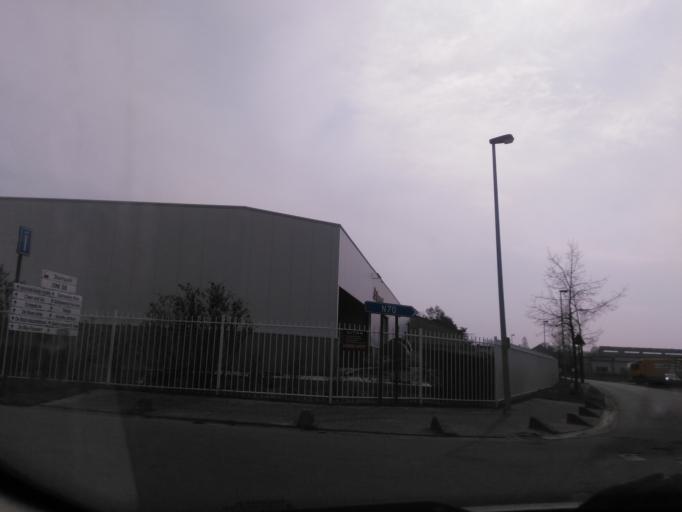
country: BE
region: Flanders
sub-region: Provincie Oost-Vlaanderen
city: Beveren
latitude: 51.1984
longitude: 4.2161
